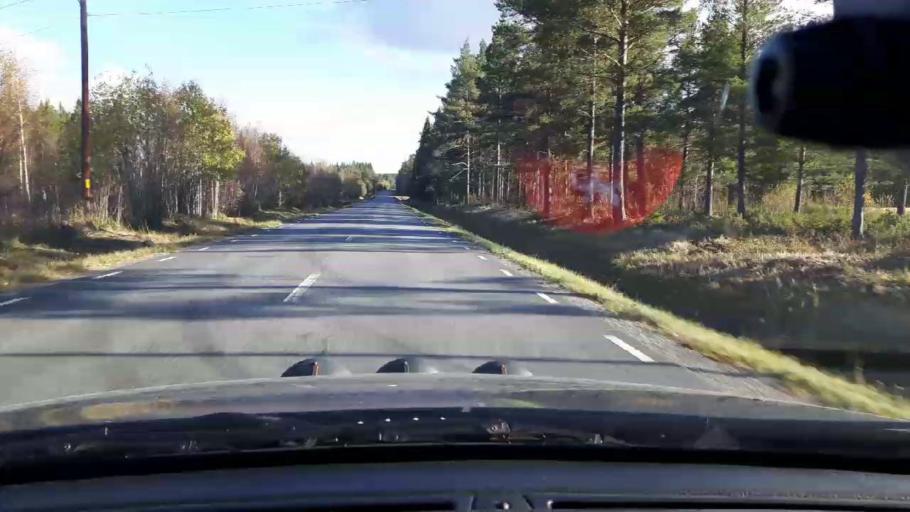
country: SE
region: Jaemtland
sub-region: Bergs Kommun
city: Hoverberg
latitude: 62.9870
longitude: 14.4368
